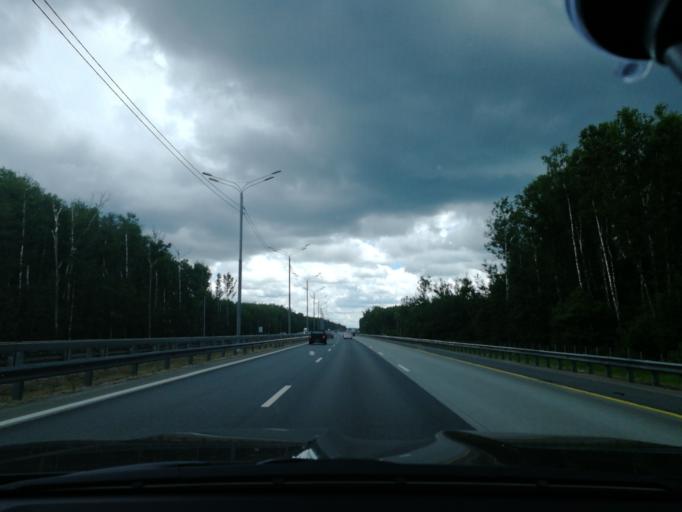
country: RU
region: Moskovskaya
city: Barybino
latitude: 55.2105
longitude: 37.8805
